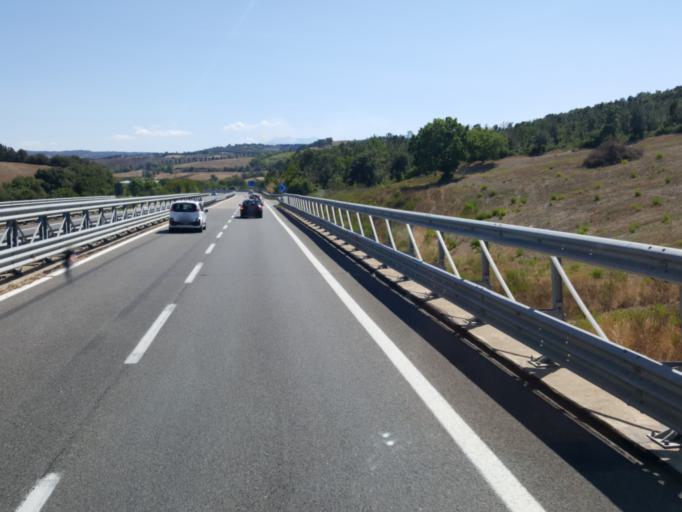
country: IT
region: Tuscany
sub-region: Provincia di Grosseto
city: Campagnatico
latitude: 42.8867
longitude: 11.2260
